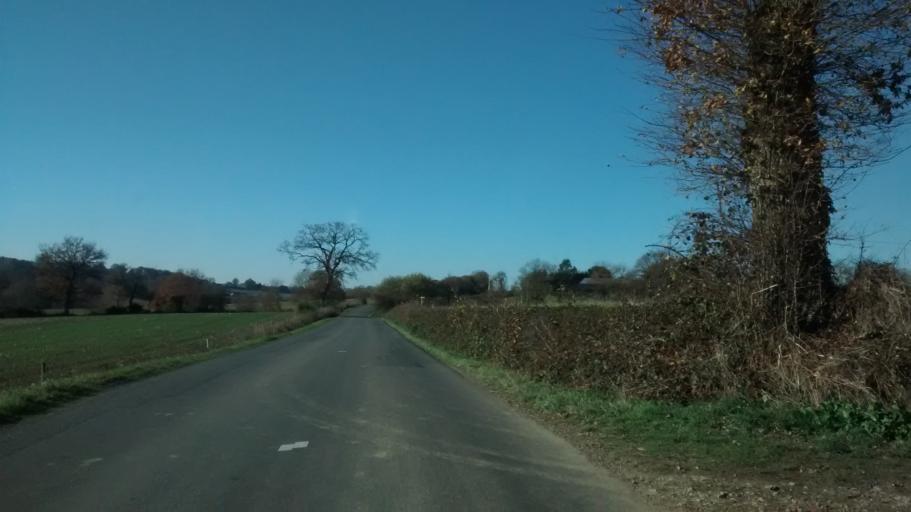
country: FR
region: Brittany
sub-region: Departement d'Ille-et-Vilaine
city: La Bouexiere
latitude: 48.1980
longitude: -1.4453
